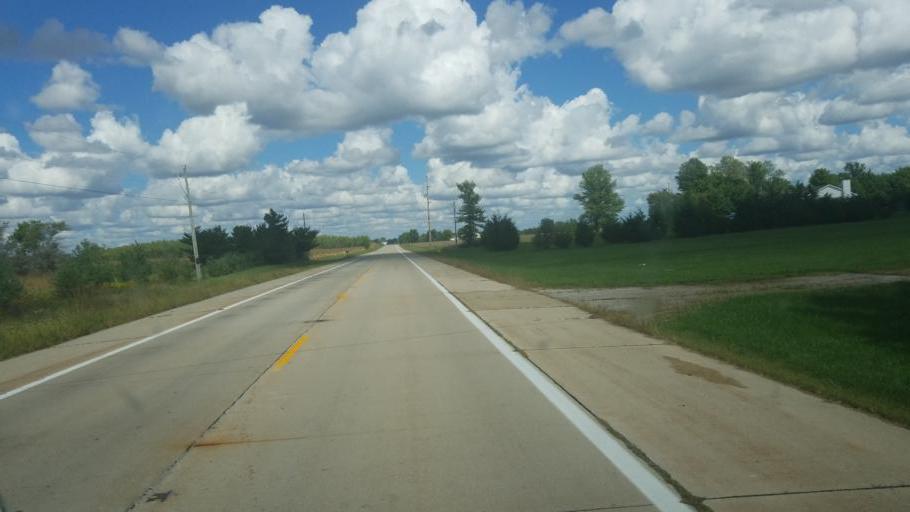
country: US
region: Ohio
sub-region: Champaign County
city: North Lewisburg
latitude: 40.3215
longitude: -83.4872
